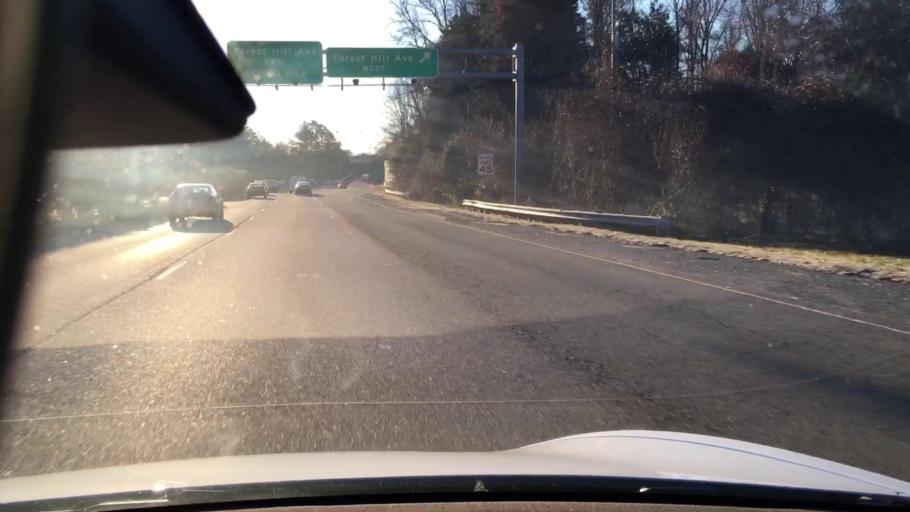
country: US
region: Virginia
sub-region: Chesterfield County
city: Bon Air
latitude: 37.5398
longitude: -77.5319
